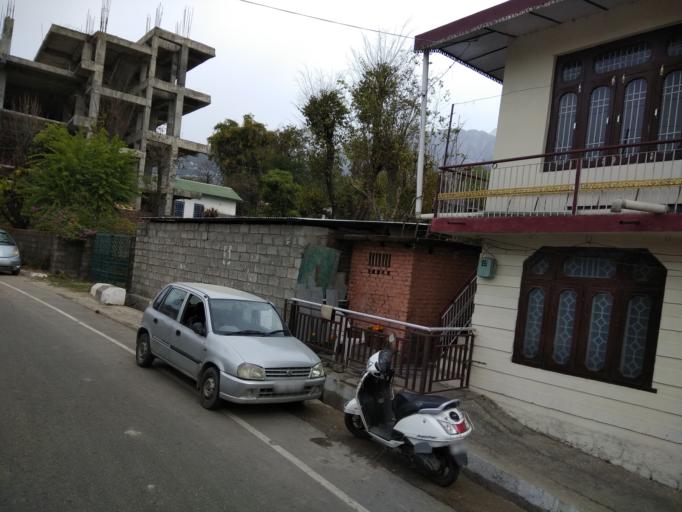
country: IN
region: Himachal Pradesh
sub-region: Kangra
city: Dharmsala
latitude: 32.2046
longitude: 76.3296
